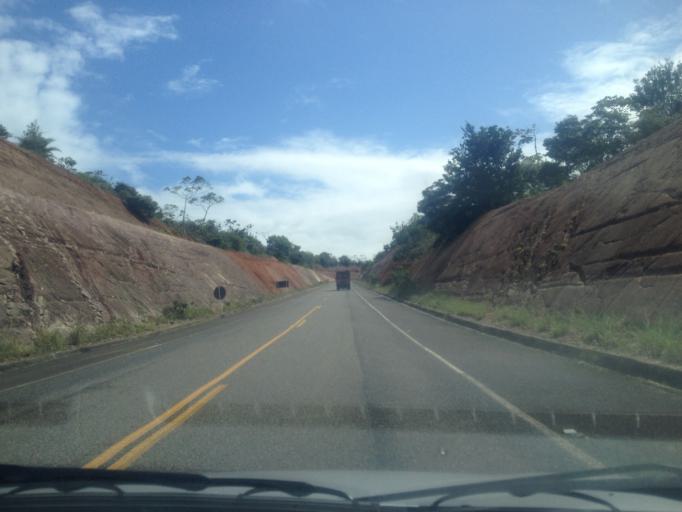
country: BR
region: Sergipe
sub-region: Indiaroba
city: Indiaroba
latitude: -11.5633
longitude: -37.5691
